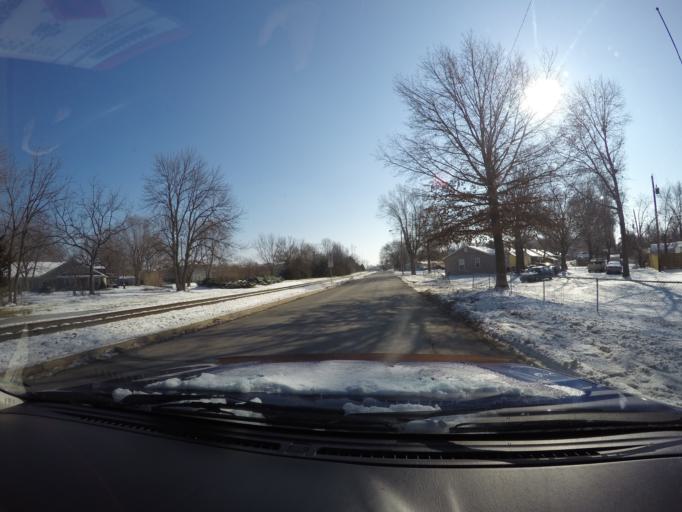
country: US
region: Kansas
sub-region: Johnson County
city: Olathe
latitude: 38.8734
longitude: -94.8187
